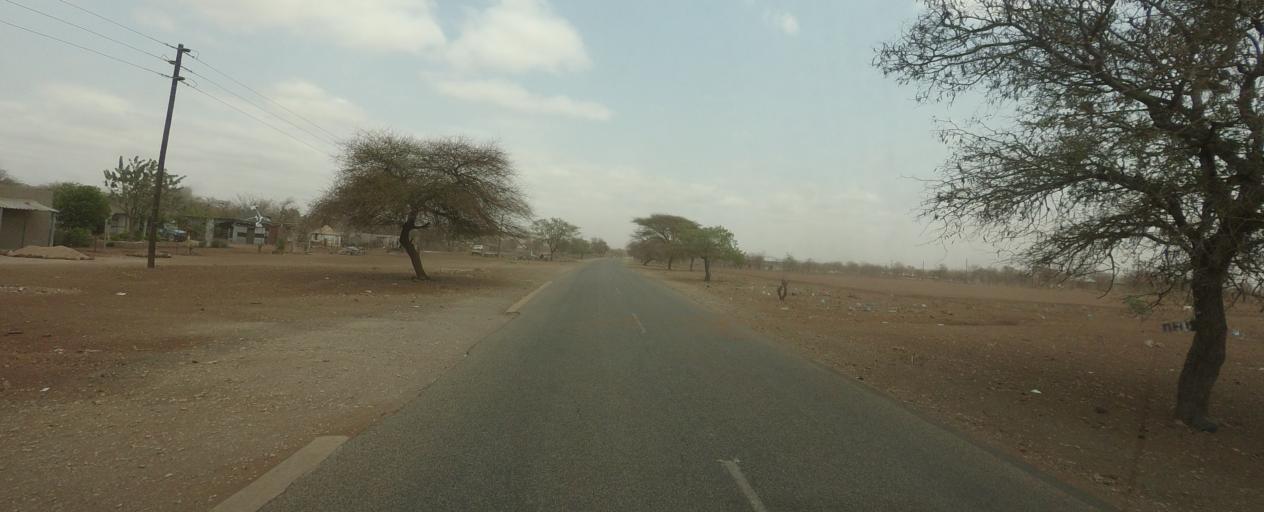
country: ZA
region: Limpopo
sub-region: Vhembe District Municipality
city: Mutale
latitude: -22.4231
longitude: 30.8867
